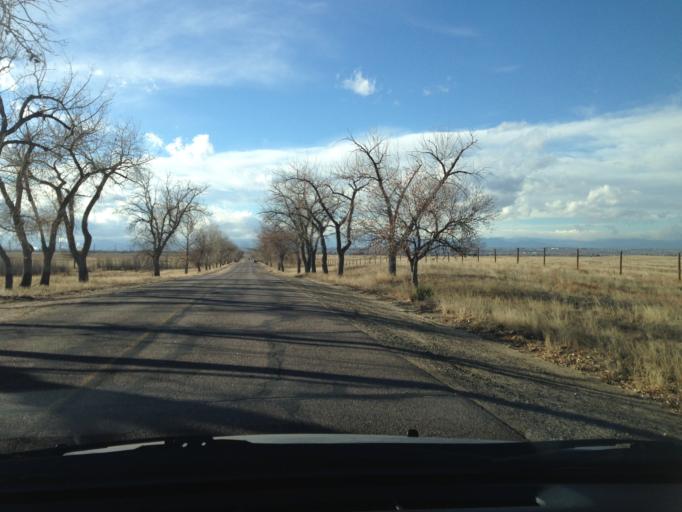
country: US
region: Colorado
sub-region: Adams County
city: Derby
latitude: 39.8273
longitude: -104.8735
